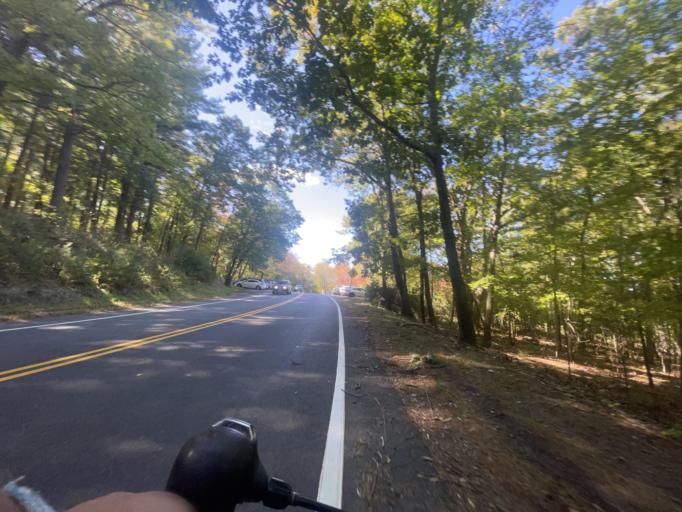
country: US
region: Massachusetts
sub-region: Norfolk County
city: Milton
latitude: 42.2263
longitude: -71.0603
